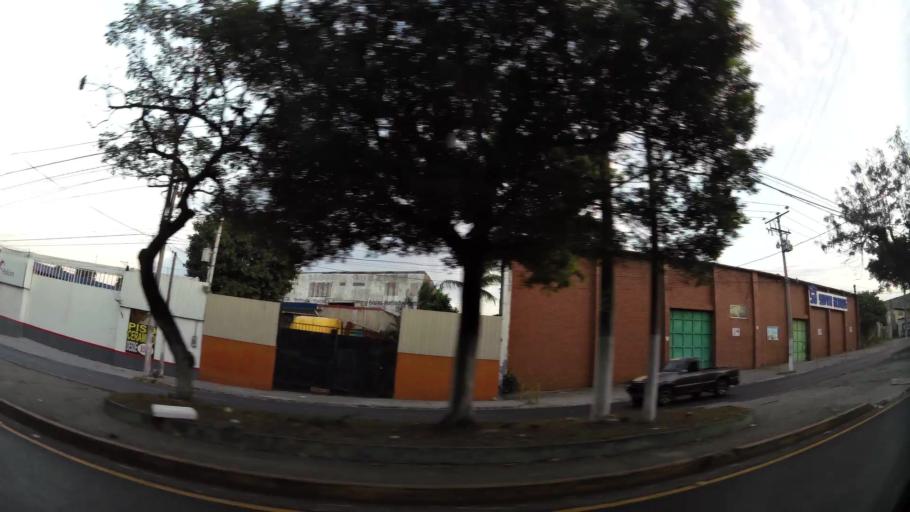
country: SV
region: San Salvador
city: San Salvador
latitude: 13.7058
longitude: -89.1794
